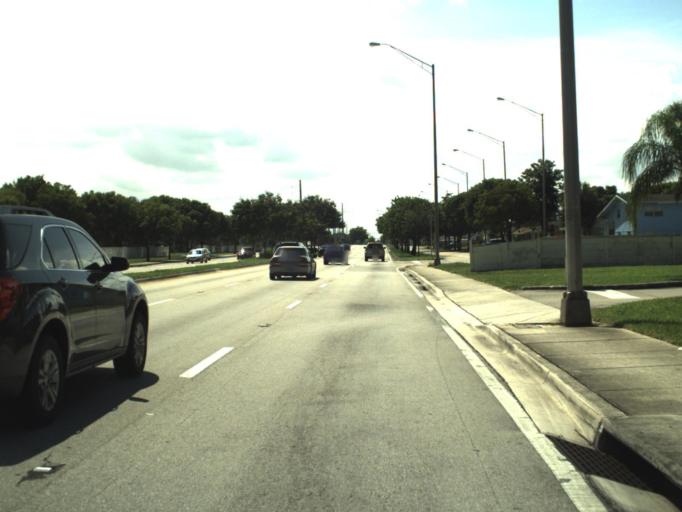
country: US
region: Florida
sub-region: Miami-Dade County
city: Carol City
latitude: 25.9404
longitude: -80.2620
